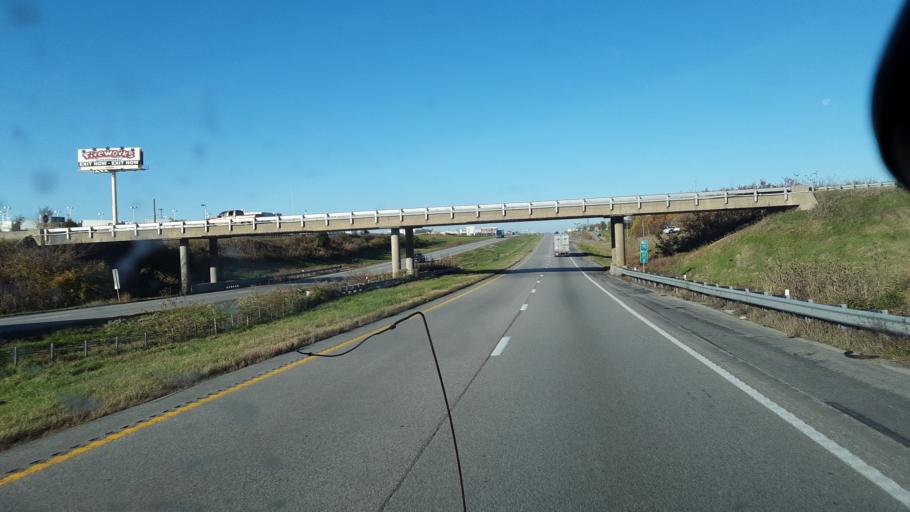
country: US
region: Missouri
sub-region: Lafayette County
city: Odessa
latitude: 39.0091
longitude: -93.9634
